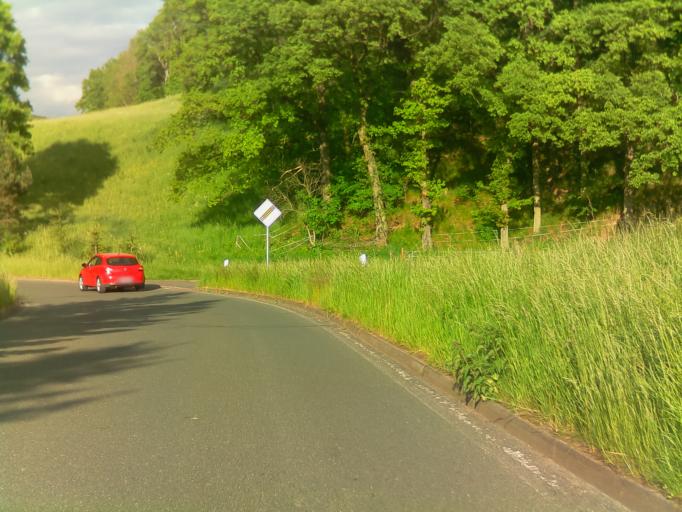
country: DE
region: Thuringia
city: Rudolstadt
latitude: 50.7002
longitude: 11.3554
